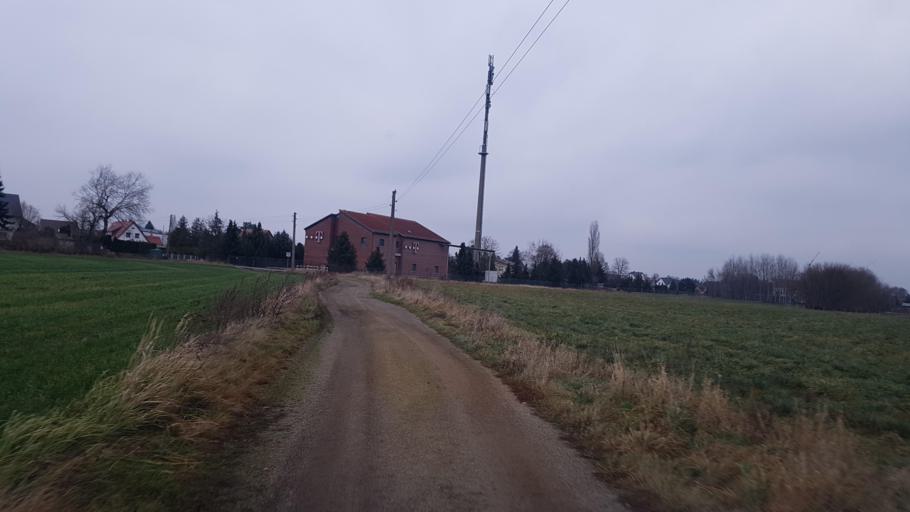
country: DE
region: Brandenburg
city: Tettau
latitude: 51.4691
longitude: 13.7317
